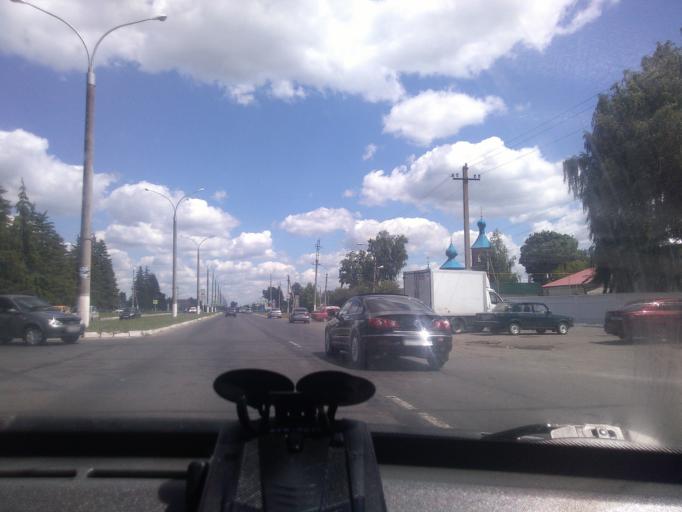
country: RU
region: Kursk
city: Pryamitsyno
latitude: 51.6572
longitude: 35.9393
